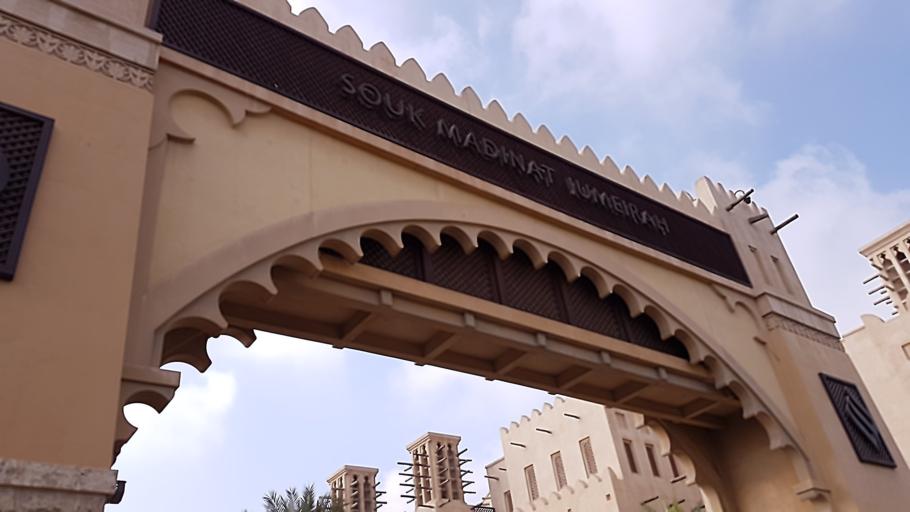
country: AE
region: Dubai
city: Dubai
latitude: 25.1332
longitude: 55.1869
